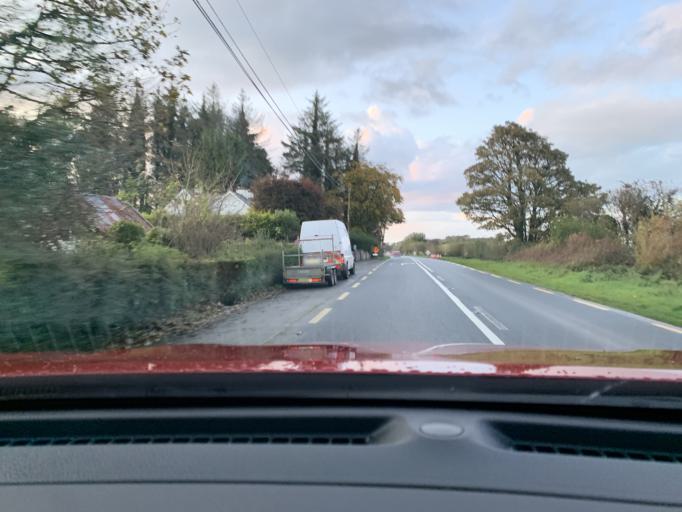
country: IE
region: Connaught
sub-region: Sligo
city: Ballymote
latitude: 54.0882
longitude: -8.3861
